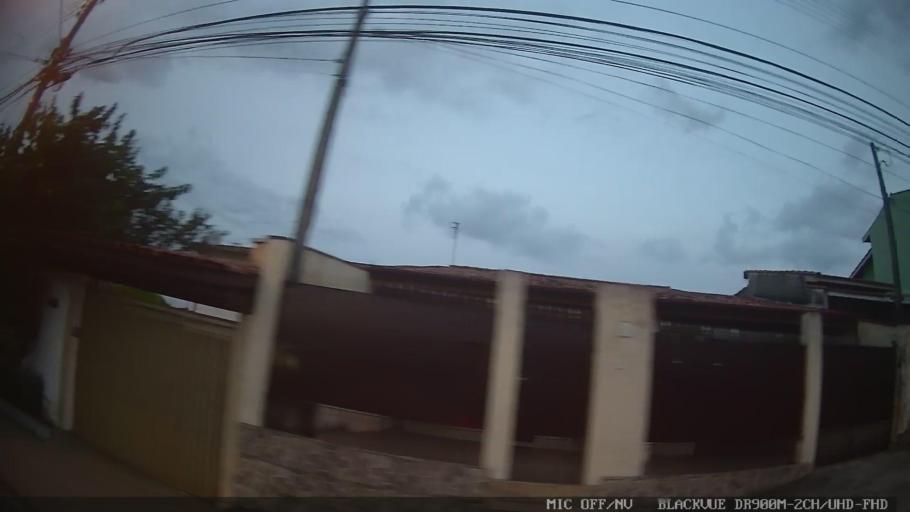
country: BR
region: Sao Paulo
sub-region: Atibaia
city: Atibaia
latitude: -23.1283
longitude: -46.5694
